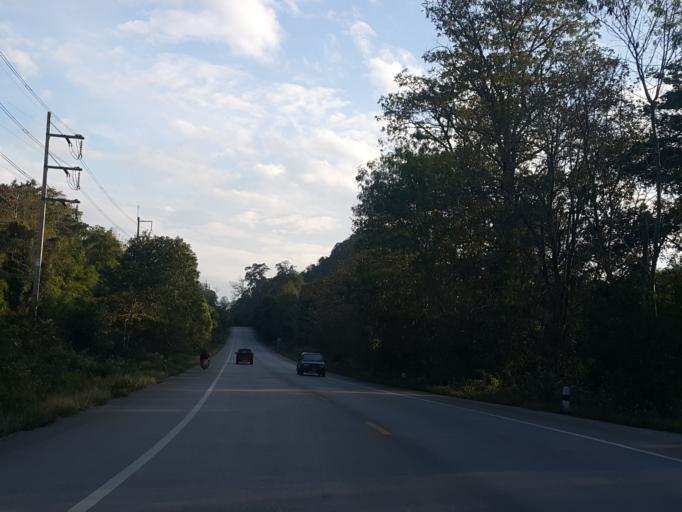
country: TH
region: Lampang
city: Lampang
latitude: 18.4947
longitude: 99.5466
